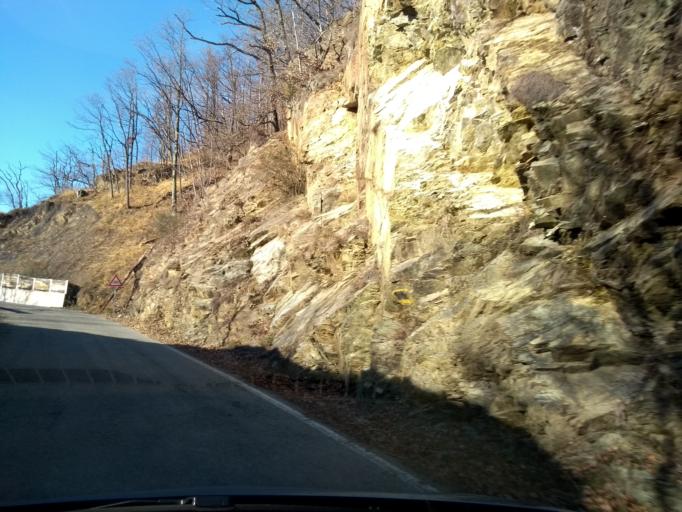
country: IT
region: Piedmont
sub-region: Provincia di Torino
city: Traves
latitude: 45.2818
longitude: 7.4319
